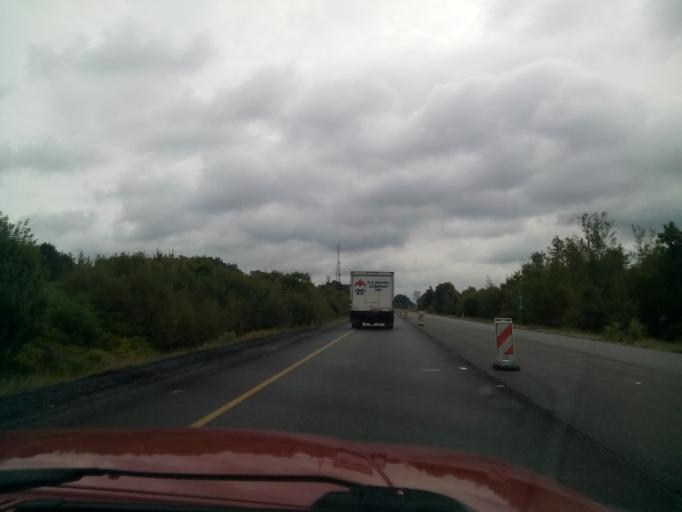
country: US
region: Pennsylvania
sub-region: Jefferson County
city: Reynoldsville
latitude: 41.1515
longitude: -78.8815
